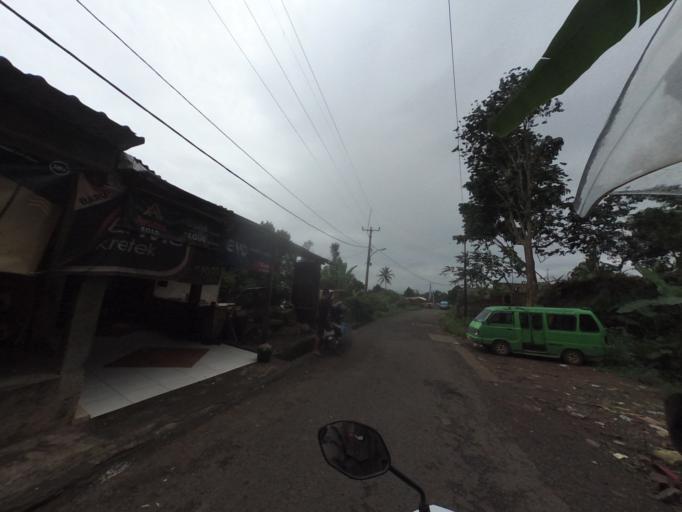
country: ID
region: West Java
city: Bogor
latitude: -6.6366
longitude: 106.7325
